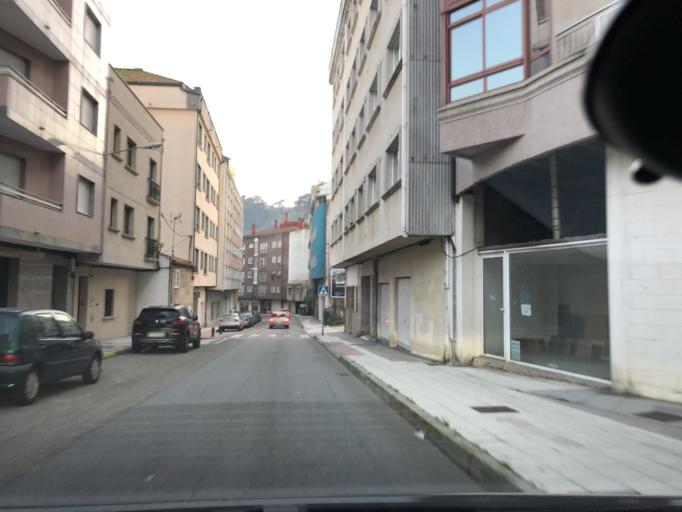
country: ES
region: Galicia
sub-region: Provincia de Pontevedra
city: Marin
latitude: 42.3918
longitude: -8.7061
